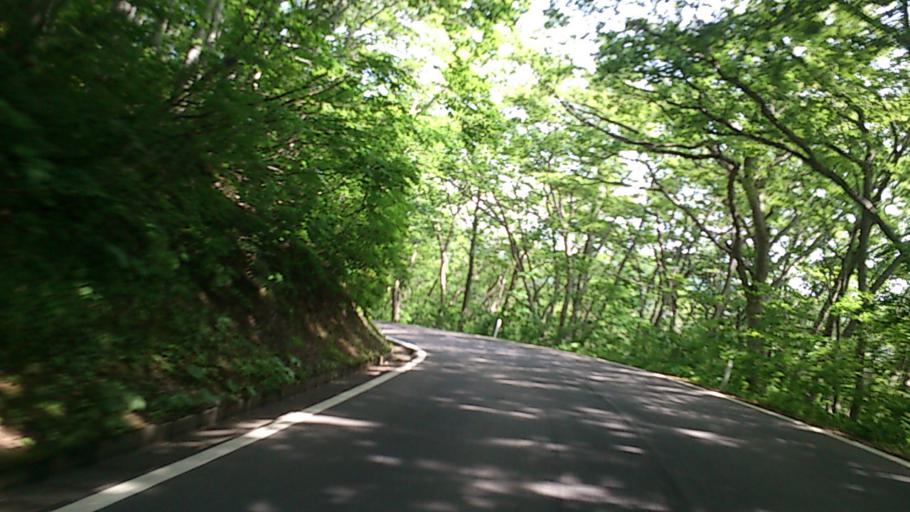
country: JP
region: Aomori
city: Aomori Shi
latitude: 40.7162
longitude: 140.8147
